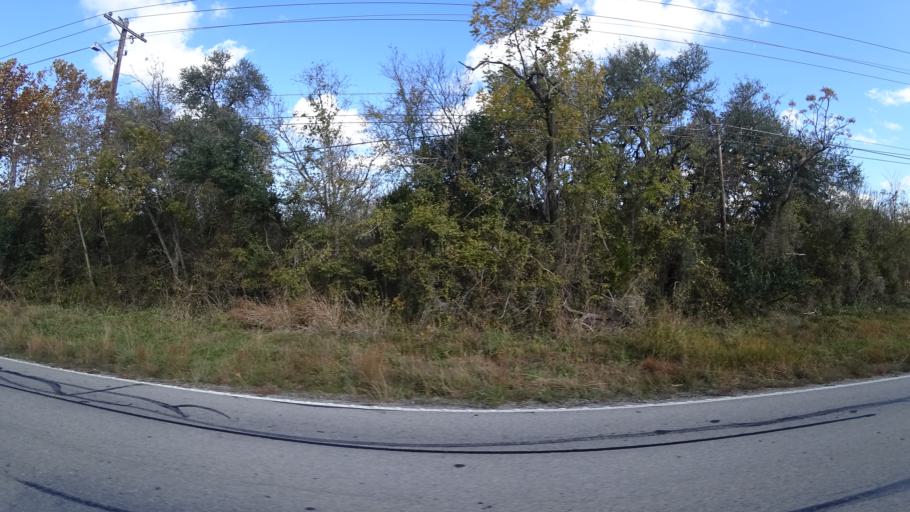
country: US
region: Texas
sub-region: Travis County
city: Shady Hollow
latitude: 30.2096
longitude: -97.9049
